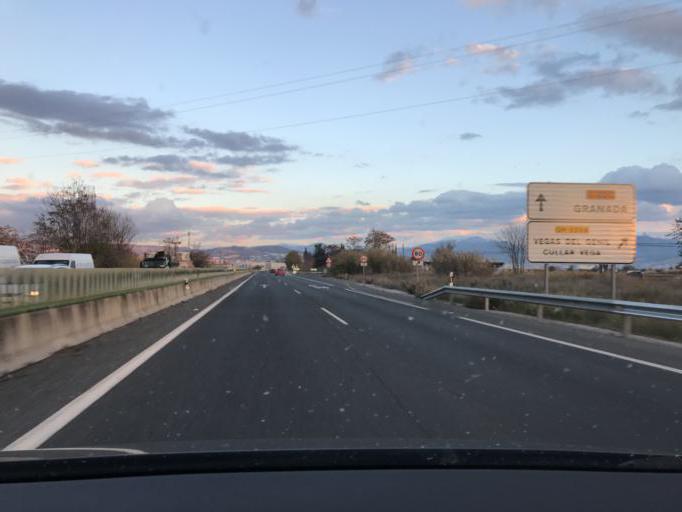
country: ES
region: Andalusia
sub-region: Provincia de Granada
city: Atarfe
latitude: 37.1923
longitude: -3.6721
